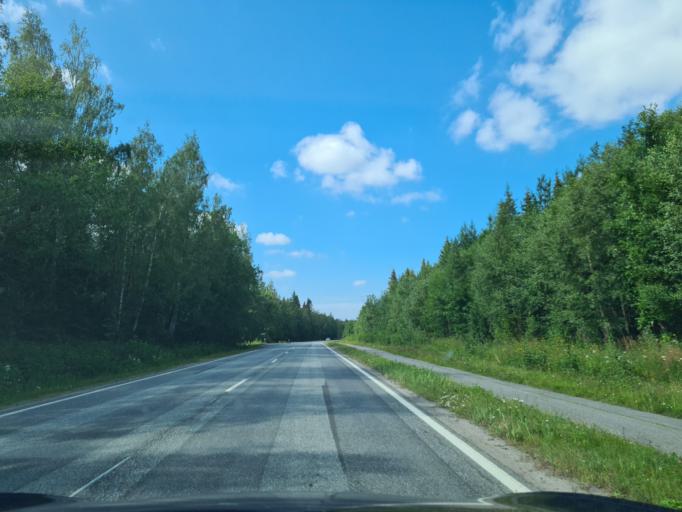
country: FI
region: Ostrobothnia
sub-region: Vaasa
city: Replot
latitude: 63.1986
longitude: 21.5386
